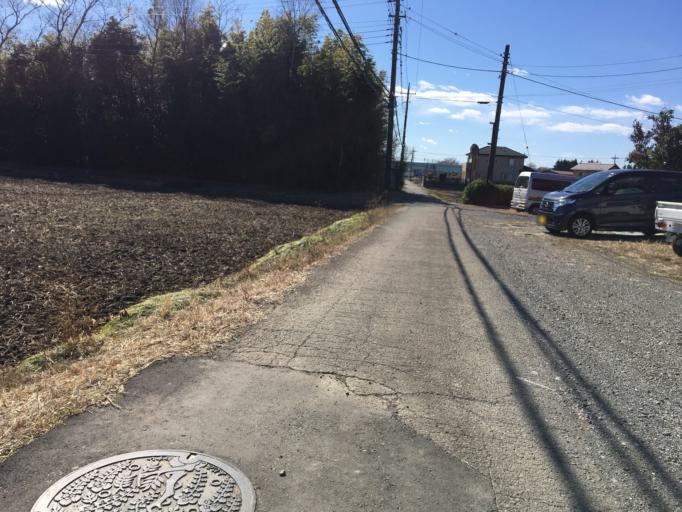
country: JP
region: Saitama
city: Shiki
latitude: 35.8497
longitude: 139.5768
